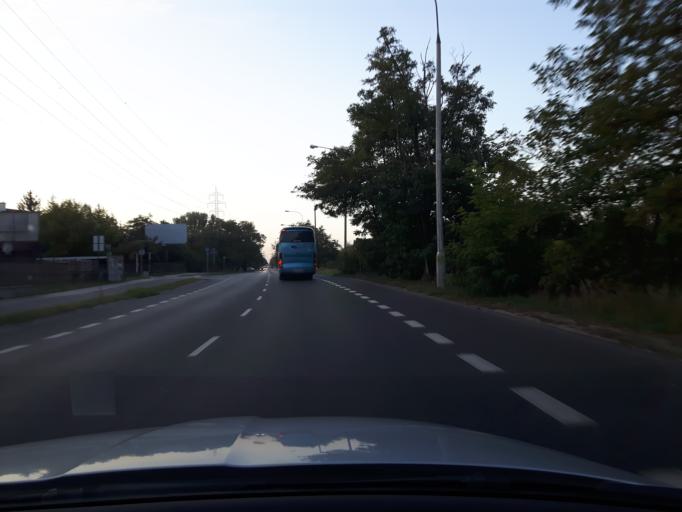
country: PL
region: Masovian Voivodeship
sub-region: Warszawa
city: Wawer
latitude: 52.2178
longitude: 21.1558
